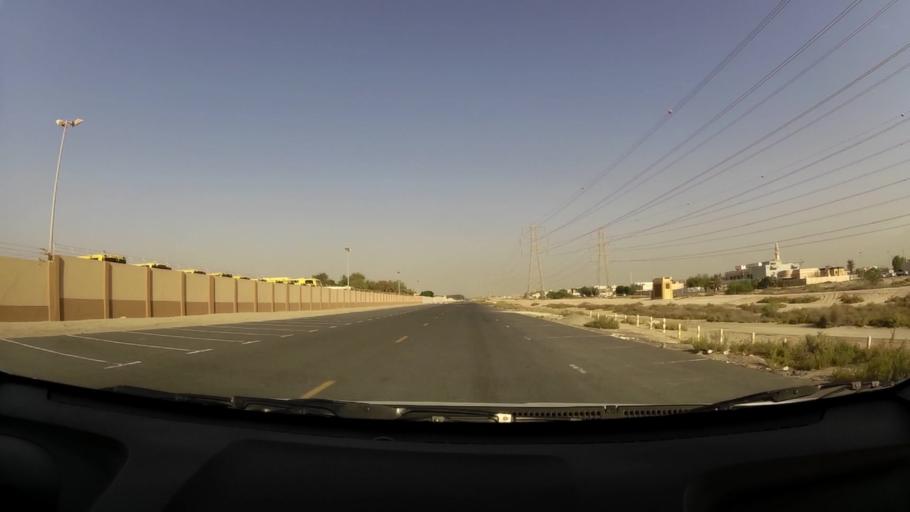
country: AE
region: Ash Shariqah
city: Sharjah
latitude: 25.2747
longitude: 55.3866
